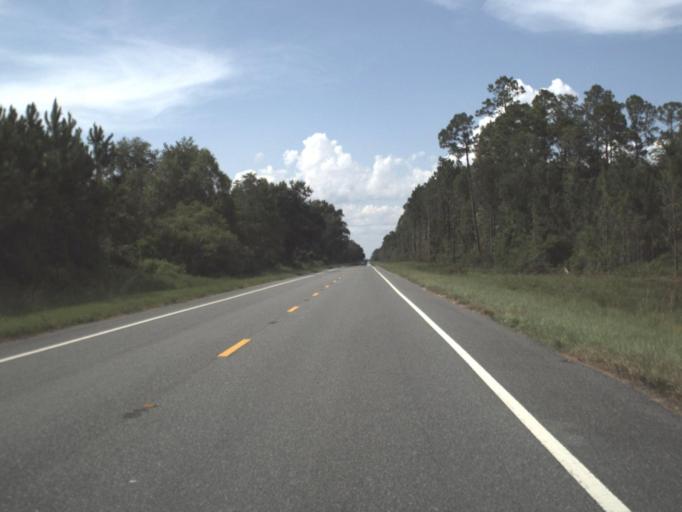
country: US
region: Florida
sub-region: Taylor County
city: Perry
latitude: 30.2375
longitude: -83.6190
